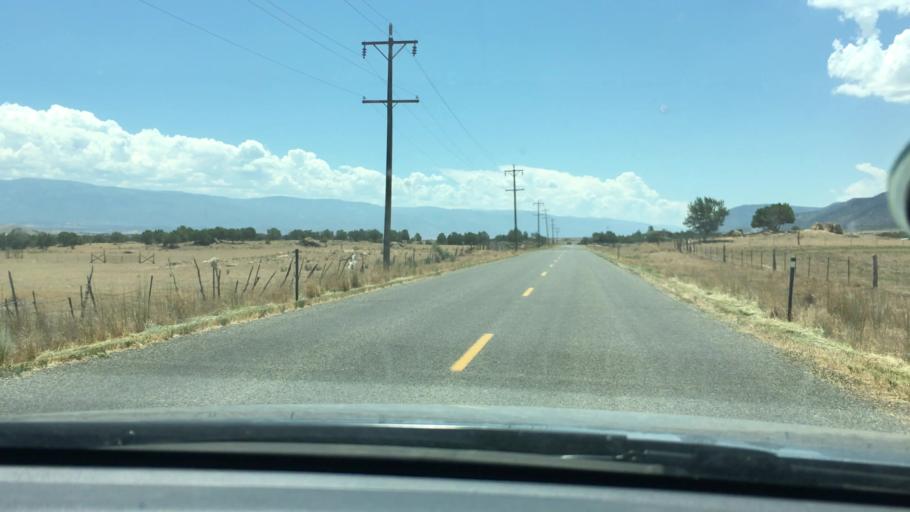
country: US
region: Utah
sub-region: Sanpete County
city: Fountain Green
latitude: 39.5955
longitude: -111.6431
